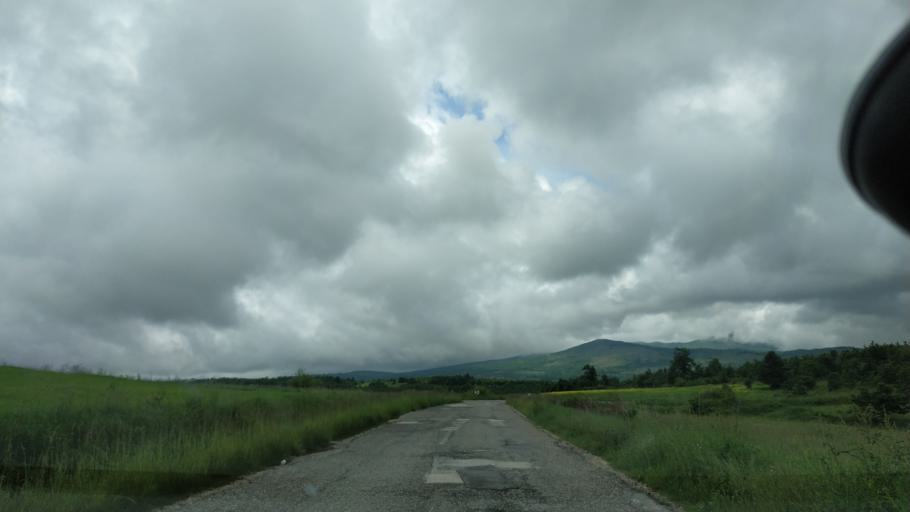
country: RS
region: Central Serbia
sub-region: Zajecarski Okrug
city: Soko Banja
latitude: 43.7012
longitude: 21.9361
